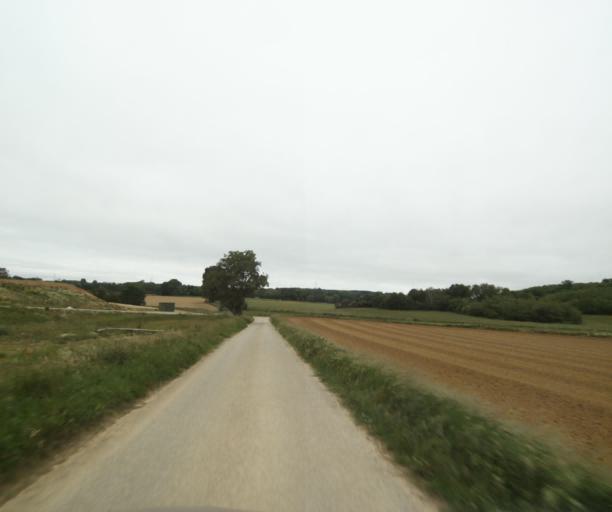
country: FR
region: Rhone-Alpes
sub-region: Departement de l'Ain
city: Miribel
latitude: 45.8433
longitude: 4.9337
